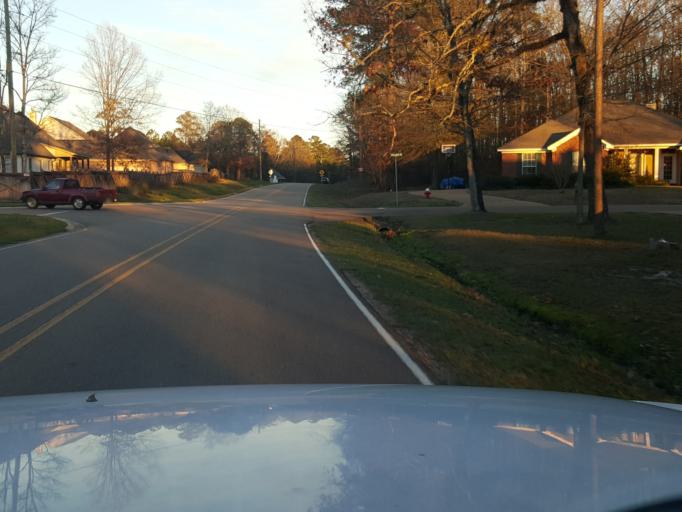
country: US
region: Mississippi
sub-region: Madison County
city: Madison
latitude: 32.4211
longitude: -90.0171
